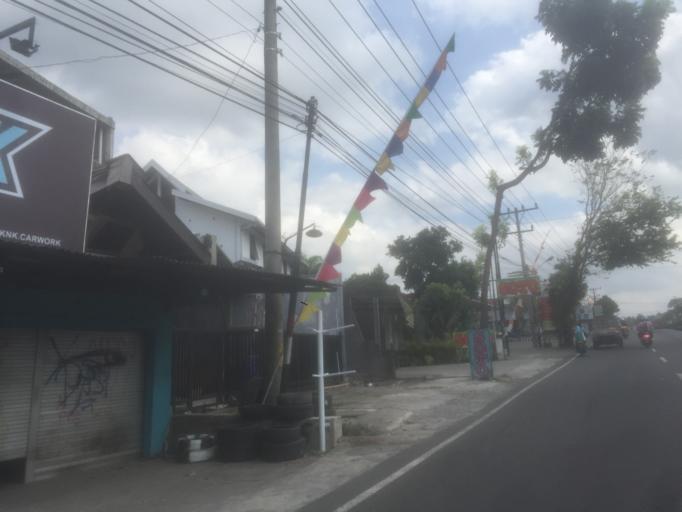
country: ID
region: Daerah Istimewa Yogyakarta
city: Sleman
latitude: -7.6775
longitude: 110.3373
